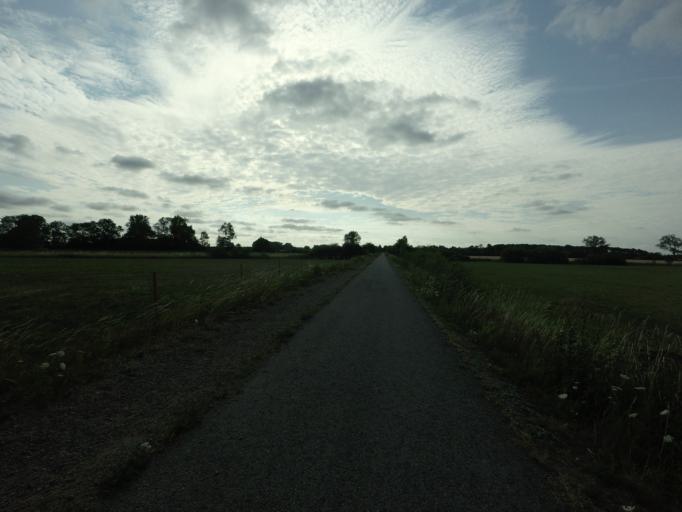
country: SE
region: Skane
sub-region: Hoganas Kommun
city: Hoganas
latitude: 56.1835
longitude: 12.6476
